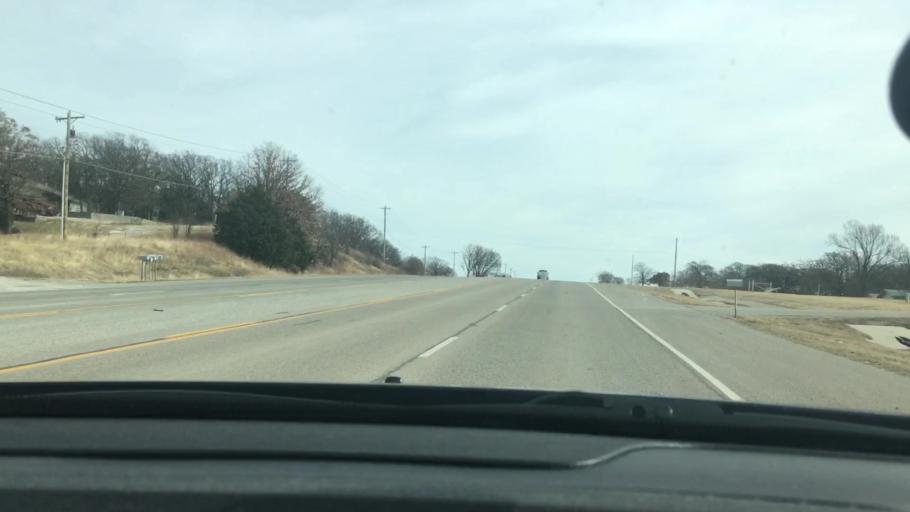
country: US
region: Oklahoma
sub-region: Carter County
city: Dickson
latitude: 34.1871
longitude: -97.0285
